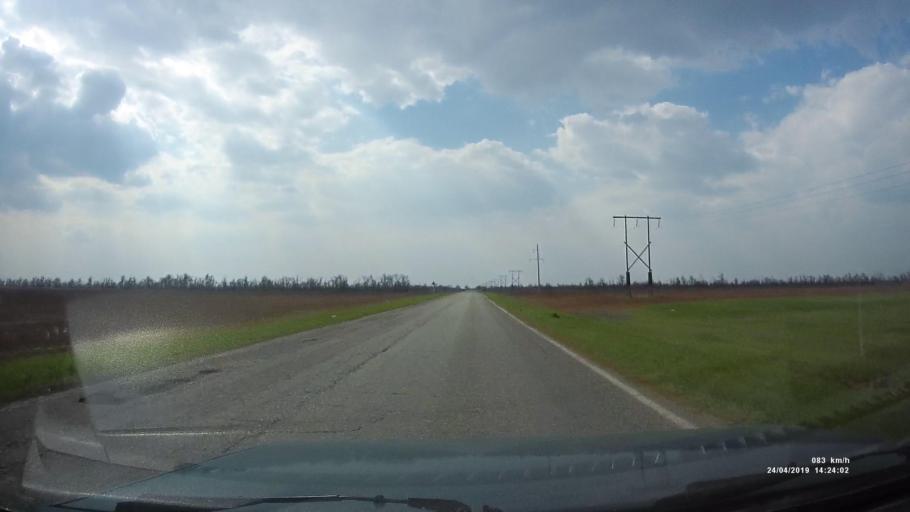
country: RU
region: Kalmykiya
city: Arshan'
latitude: 46.3266
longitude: 44.1055
